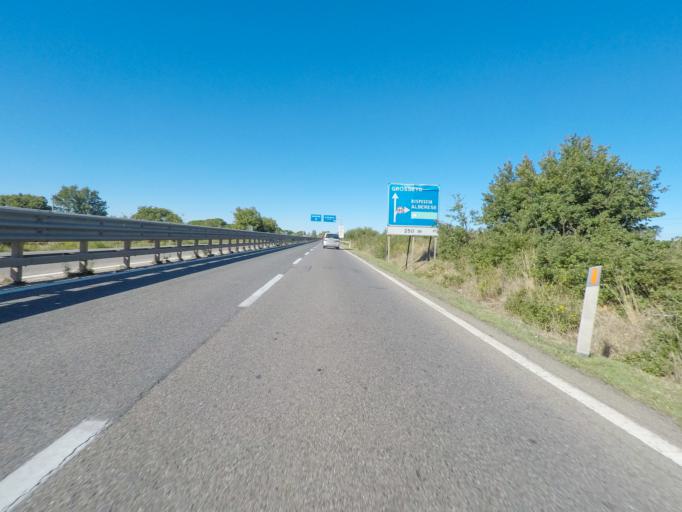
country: IT
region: Tuscany
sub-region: Provincia di Grosseto
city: Grosseto
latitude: 42.7004
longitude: 11.1374
